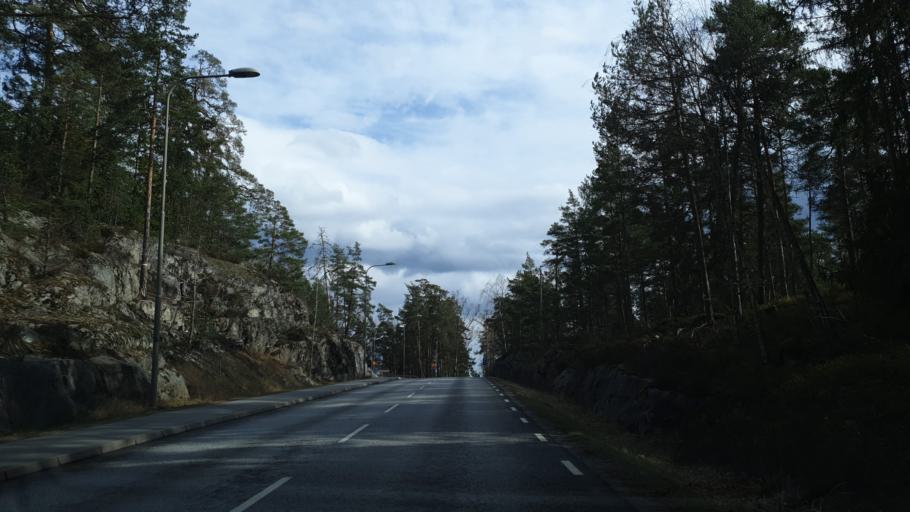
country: SE
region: Stockholm
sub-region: Nacka Kommun
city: Saltsjobaden
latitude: 59.2611
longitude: 18.3187
